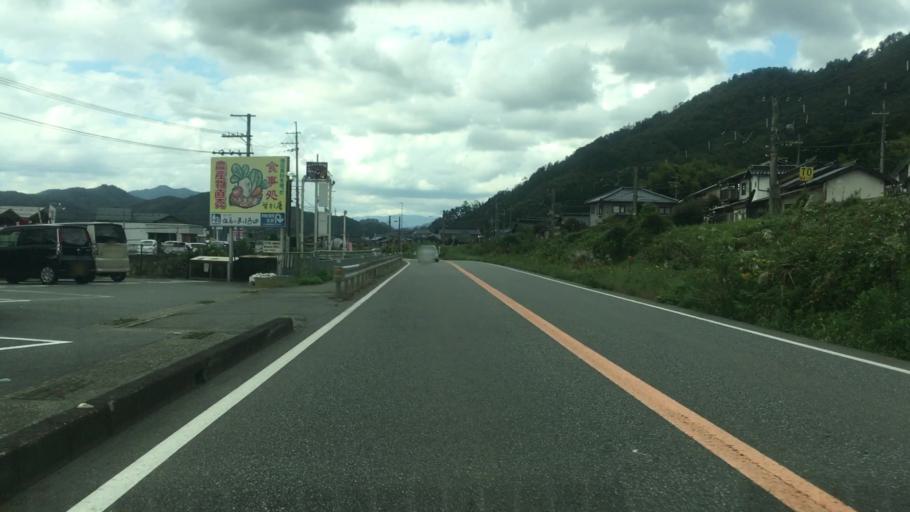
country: JP
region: Hyogo
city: Toyooka
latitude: 35.3253
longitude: 134.8767
